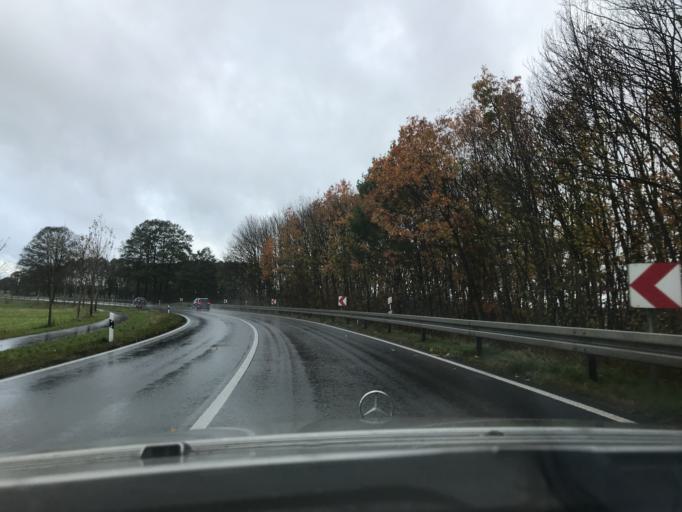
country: DE
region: Brandenburg
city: Beelitz
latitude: 52.2316
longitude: 13.0305
